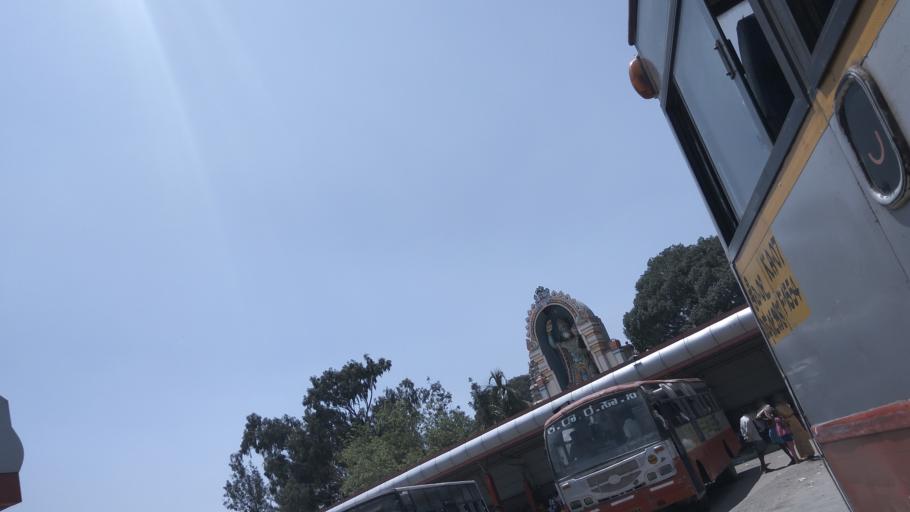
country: IN
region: Karnataka
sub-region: Kolar
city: Mulbagal
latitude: 13.1665
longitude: 78.3940
